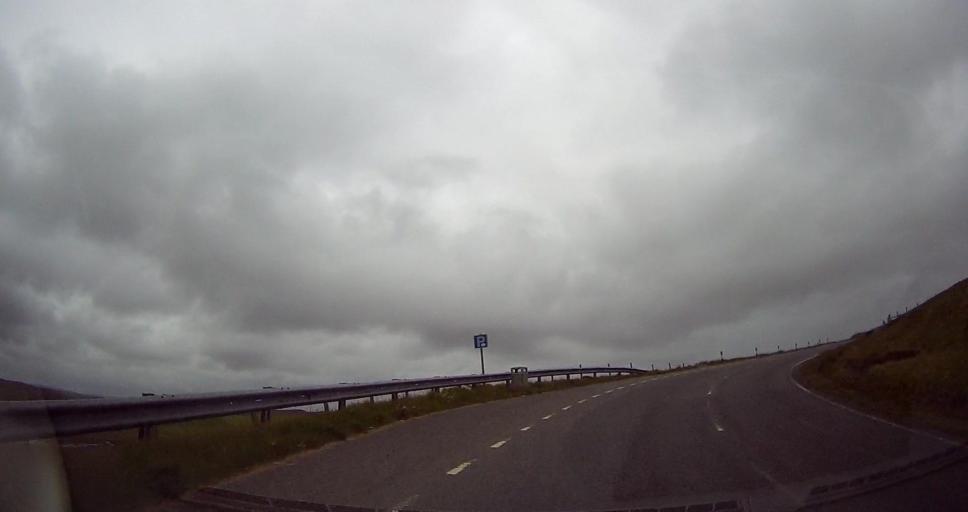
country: GB
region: Scotland
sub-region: Shetland Islands
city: Lerwick
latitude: 60.2556
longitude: -1.4065
